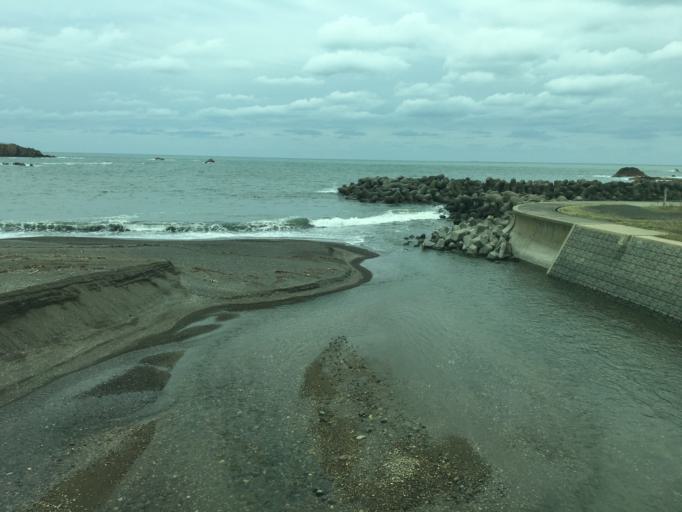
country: JP
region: Akita
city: Noshiromachi
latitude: 40.6551
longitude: 139.9380
